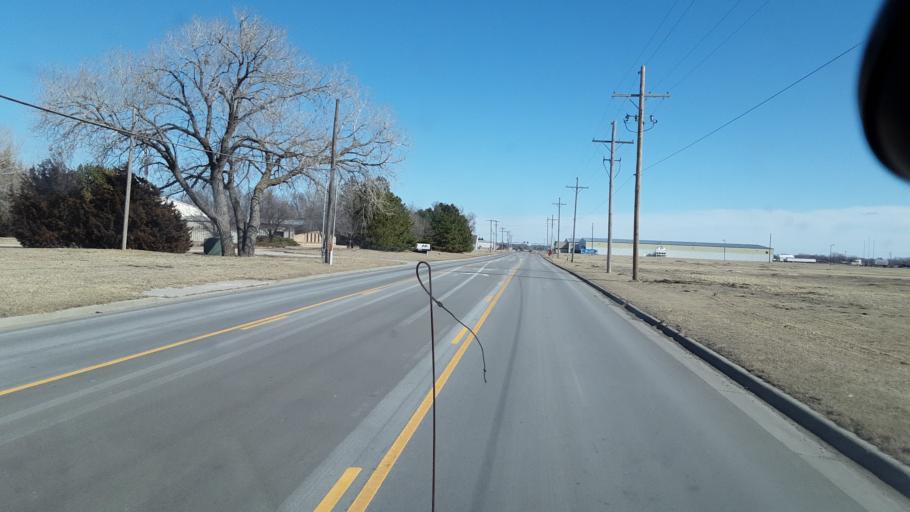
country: US
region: Kansas
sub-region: Reno County
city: Hutchinson
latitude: 38.0576
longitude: -97.8731
